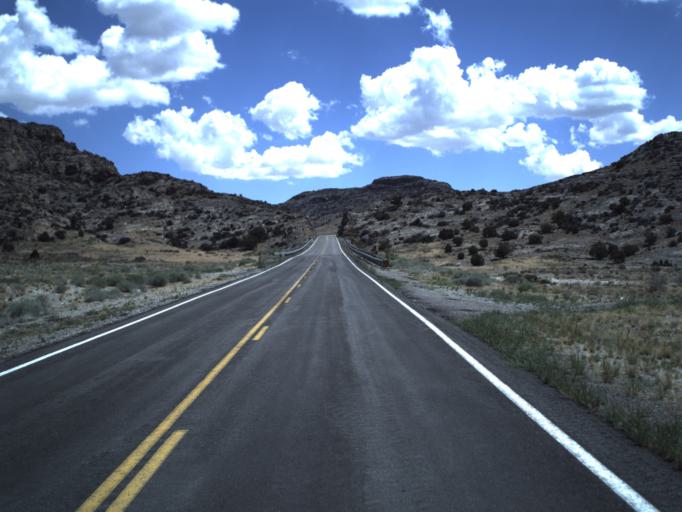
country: US
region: Utah
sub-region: Beaver County
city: Milford
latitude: 39.0723
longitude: -113.6618
